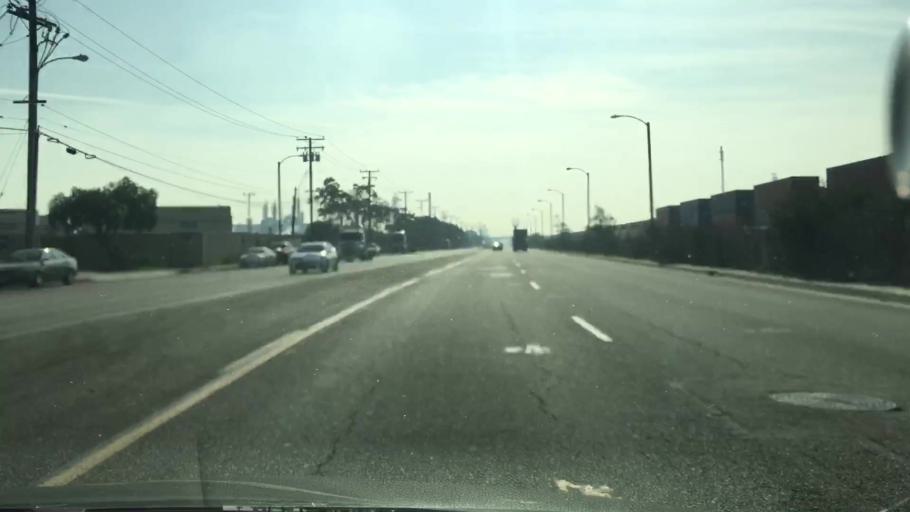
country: US
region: California
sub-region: Los Angeles County
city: Carson
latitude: 33.8204
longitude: -118.2301
